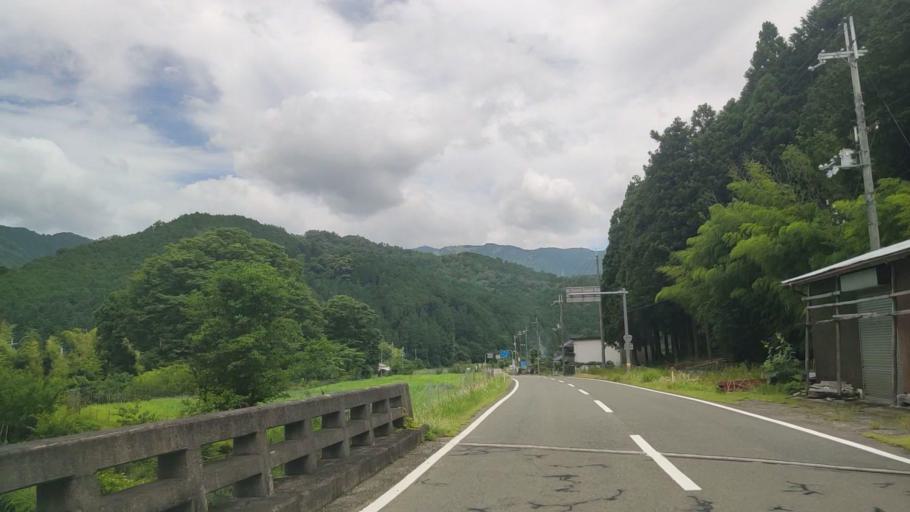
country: JP
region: Kyoto
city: Fukuchiyama
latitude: 35.2341
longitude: 134.9431
